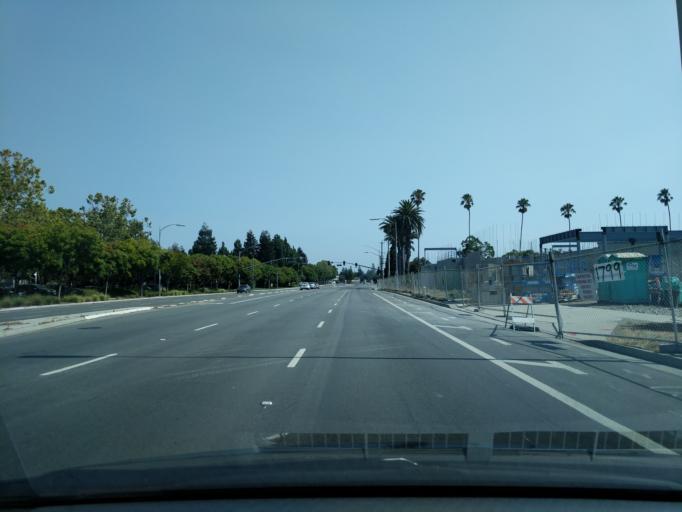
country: US
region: California
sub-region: Santa Clara County
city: Milpitas
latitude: 37.3868
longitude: -121.8988
